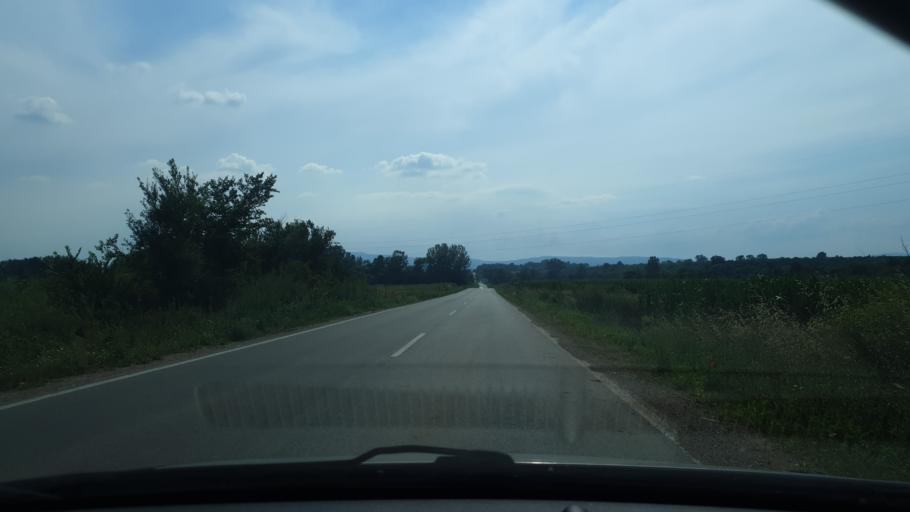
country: RS
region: Central Serbia
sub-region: Pomoravski Okrug
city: Cuprija
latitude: 43.9488
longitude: 21.4336
